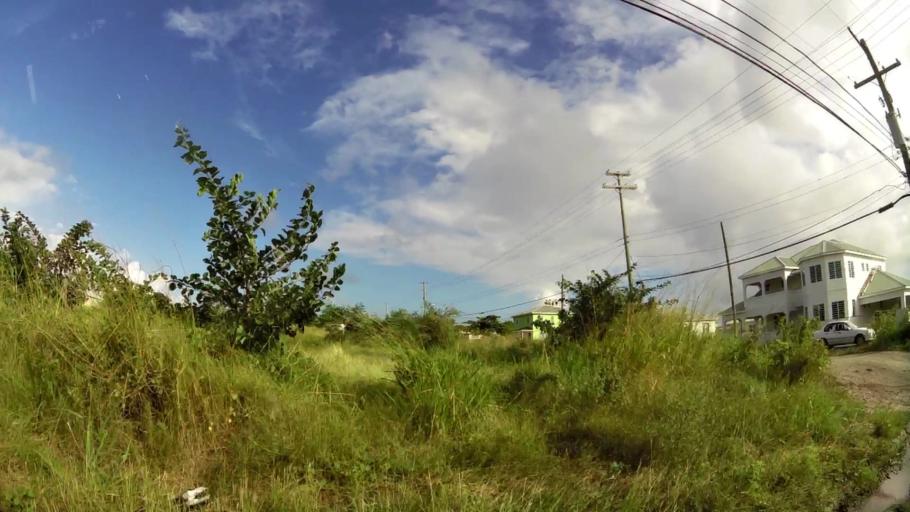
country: AG
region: Saint John
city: Saint John's
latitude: 17.1289
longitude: -61.8275
